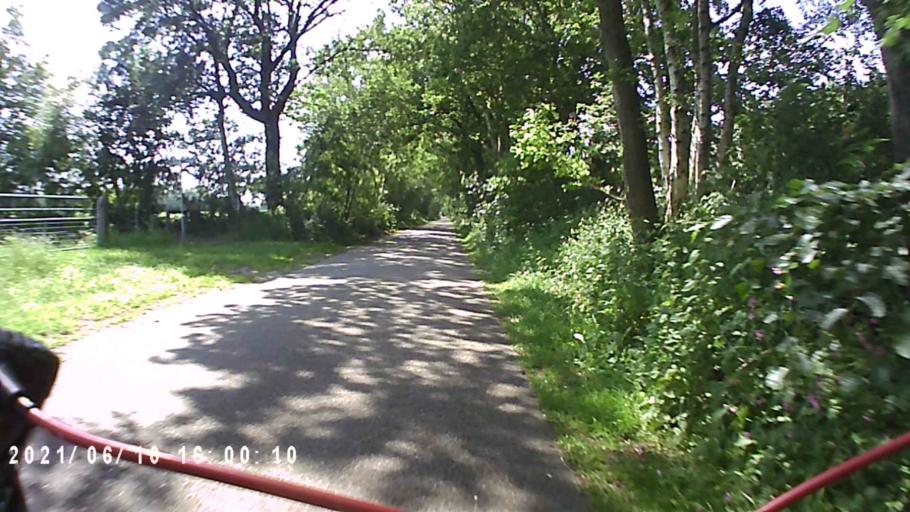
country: NL
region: Friesland
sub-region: Gemeente Achtkarspelen
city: Kootstertille
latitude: 53.1922
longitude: 6.0820
